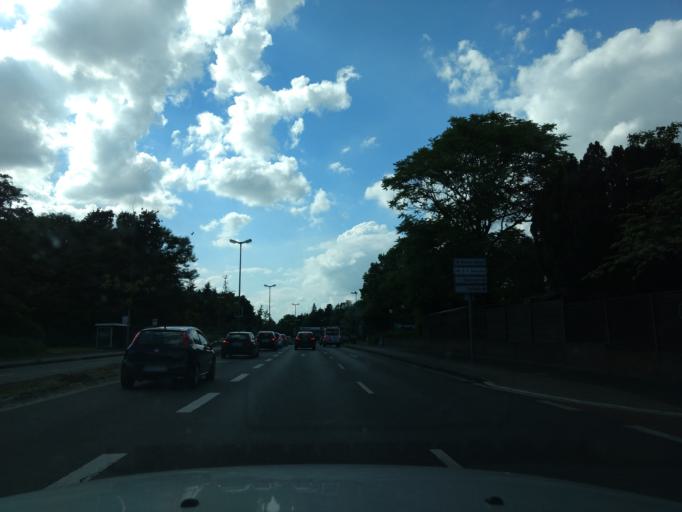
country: DE
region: North Rhine-Westphalia
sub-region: Regierungsbezirk Dusseldorf
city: Neuss
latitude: 51.1831
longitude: 6.6791
